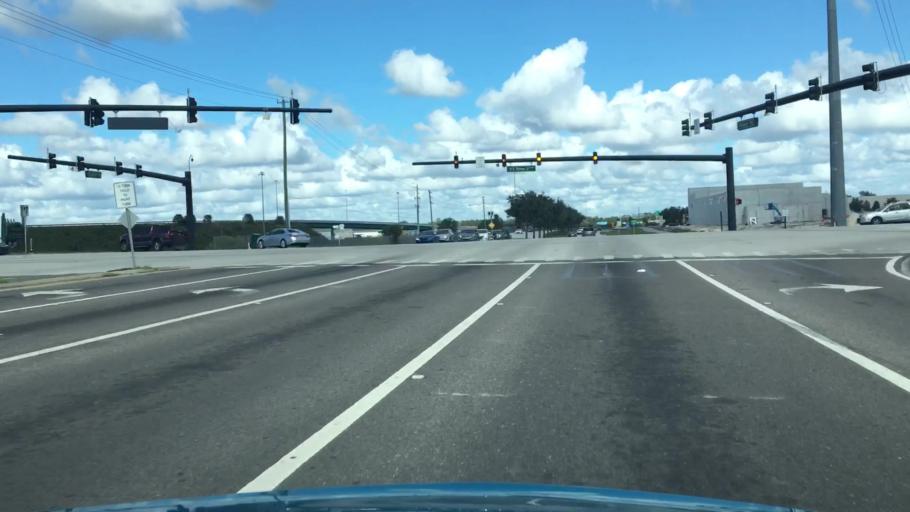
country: US
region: Florida
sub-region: Seminole County
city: Heathrow
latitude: 28.7861
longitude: -81.3472
